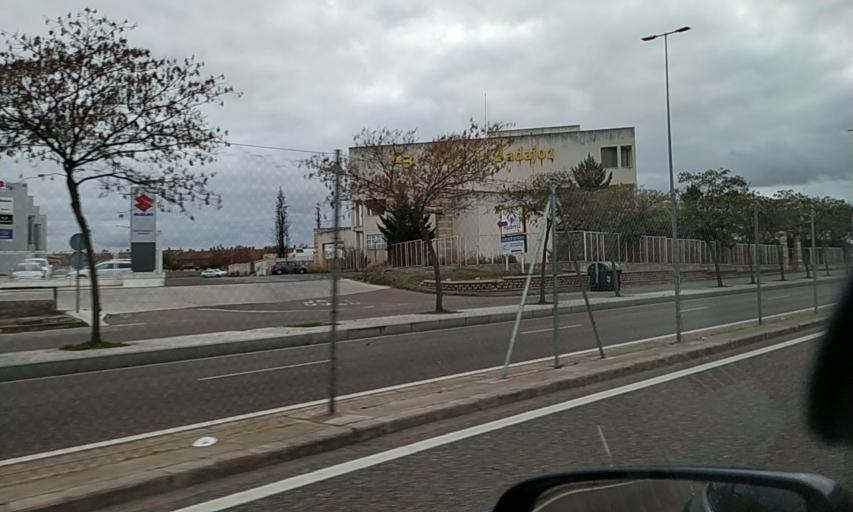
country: ES
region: Extremadura
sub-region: Provincia de Badajoz
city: Badajoz
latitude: 38.8772
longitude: -6.9485
